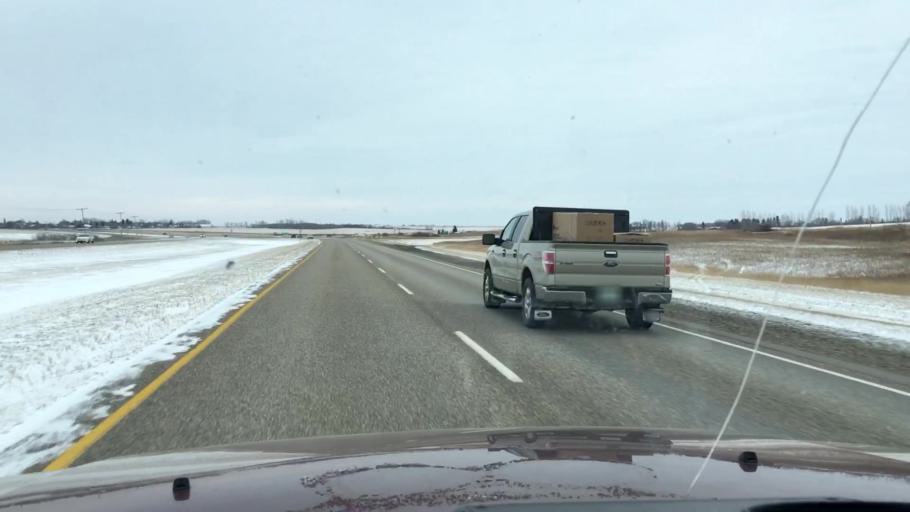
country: CA
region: Saskatchewan
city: Moose Jaw
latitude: 50.9520
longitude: -105.7085
